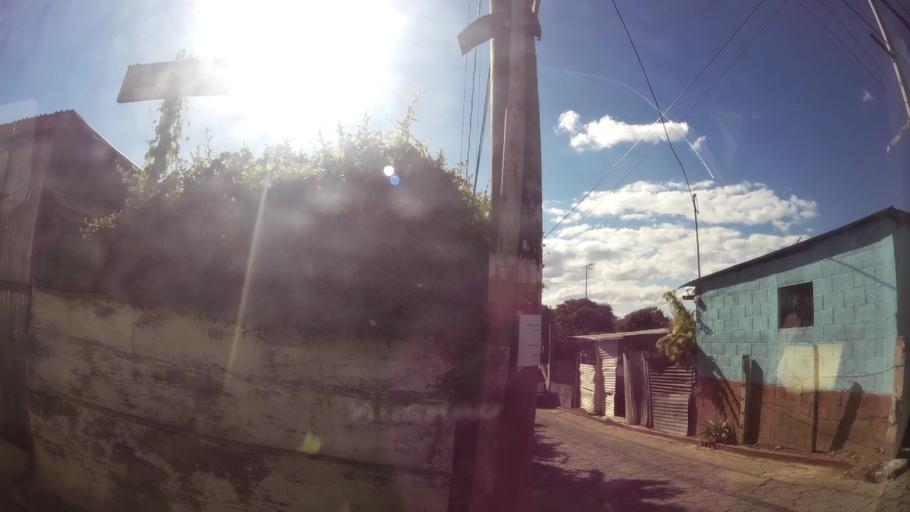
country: GT
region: Sacatepequez
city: Santa Lucia Milpas Altas
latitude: 14.5757
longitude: -90.6792
